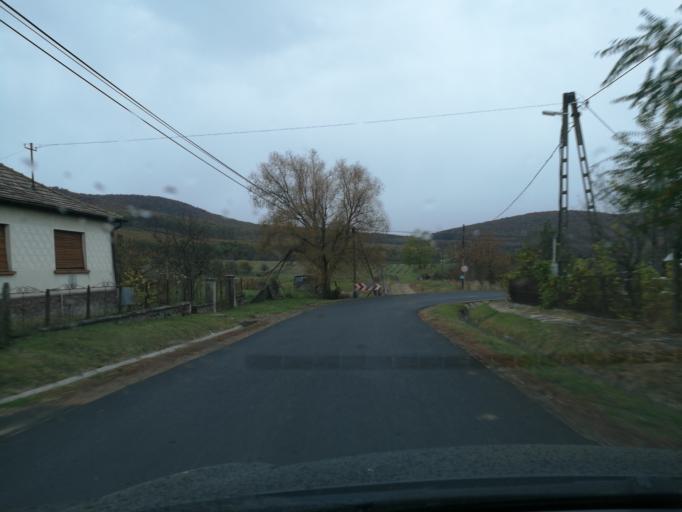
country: HU
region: Nograd
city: Paszto
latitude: 47.9770
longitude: 19.6387
